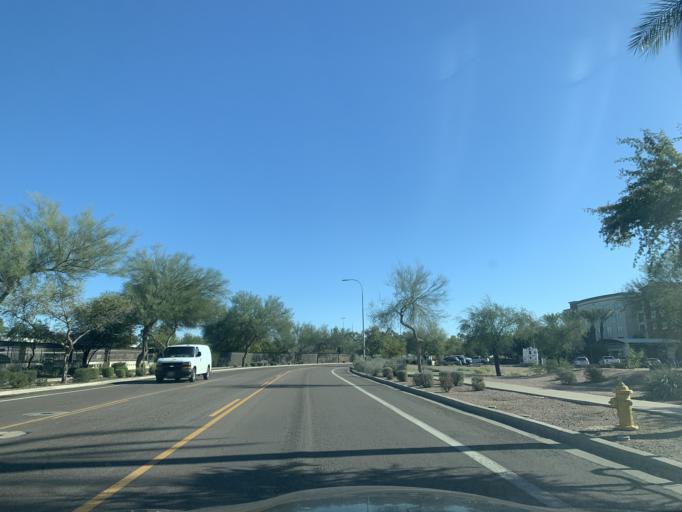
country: US
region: Arizona
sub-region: Maricopa County
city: Tempe Junction
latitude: 33.4197
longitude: -111.9802
